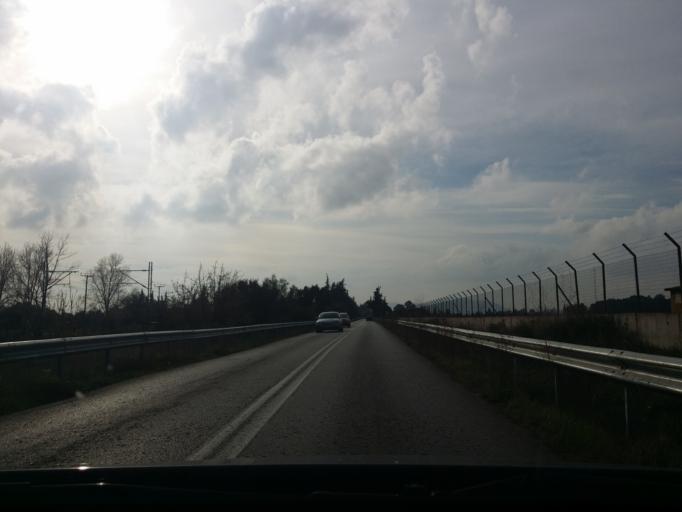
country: GR
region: Attica
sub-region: Nomarchia Anatolikis Attikis
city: Varybobi
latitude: 38.1034
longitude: 23.7855
